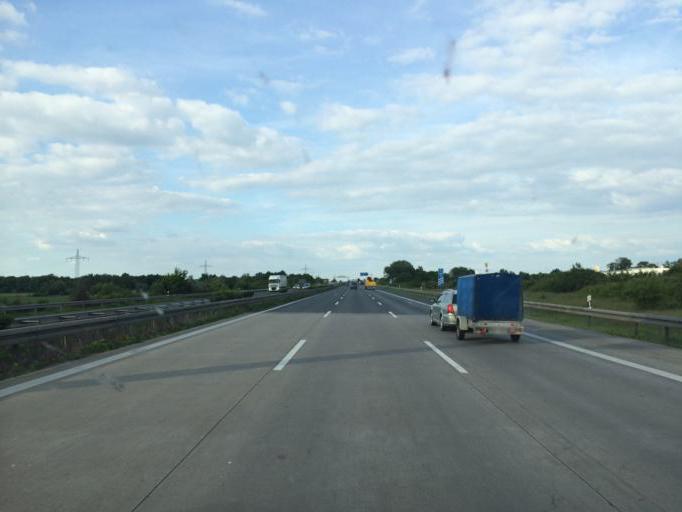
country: DE
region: Saxony-Anhalt
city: Barleben
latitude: 52.2058
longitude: 11.6557
